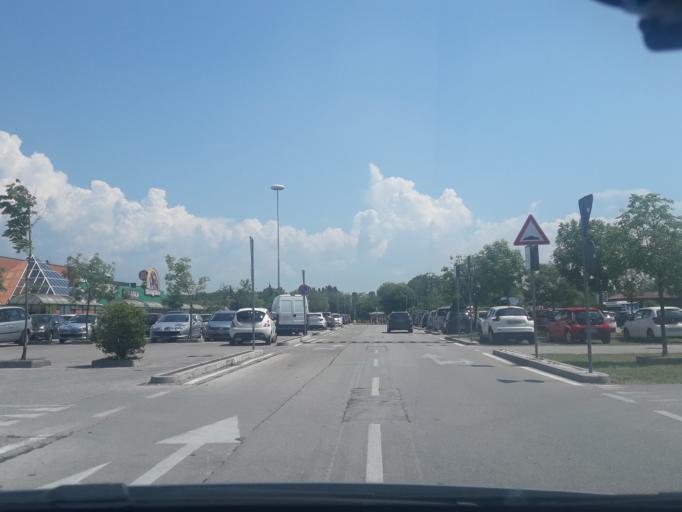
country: IT
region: Friuli Venezia Giulia
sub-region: Provincia di Udine
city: Passons
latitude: 46.0840
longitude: 13.1808
